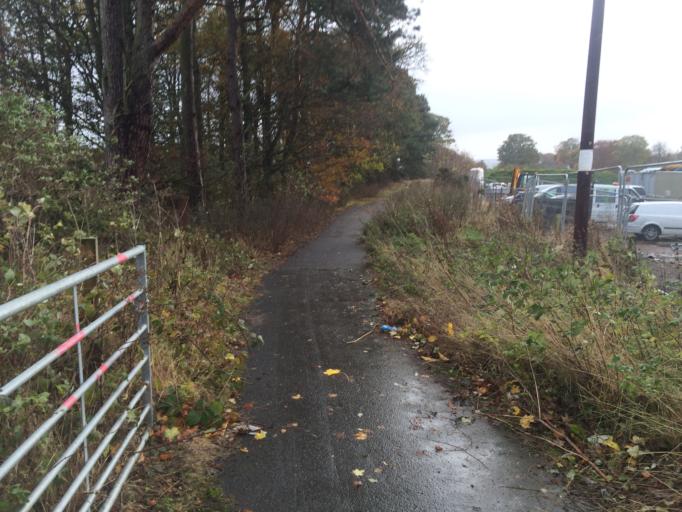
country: GB
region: Scotland
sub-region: Highland
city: Alness
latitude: 57.6928
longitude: -4.2447
